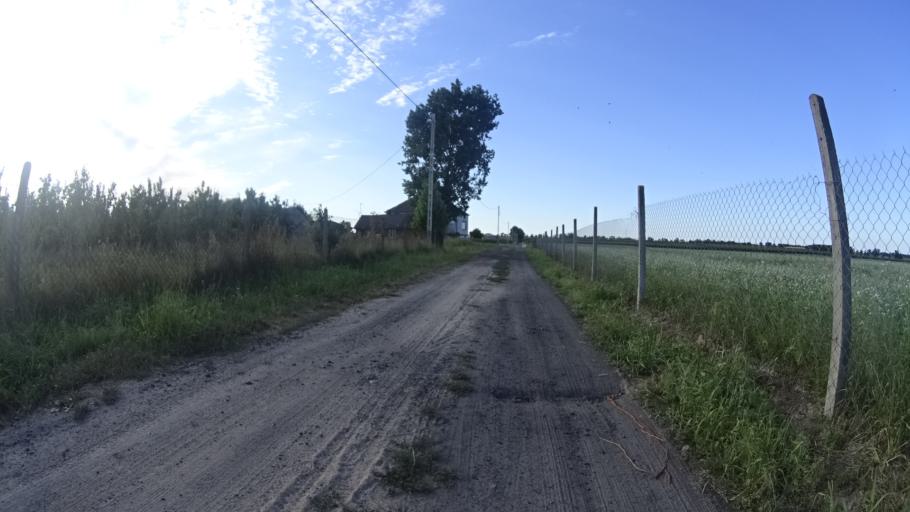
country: PL
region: Masovian Voivodeship
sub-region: Powiat bialobrzeski
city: Wysmierzyce
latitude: 51.6786
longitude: 20.8174
